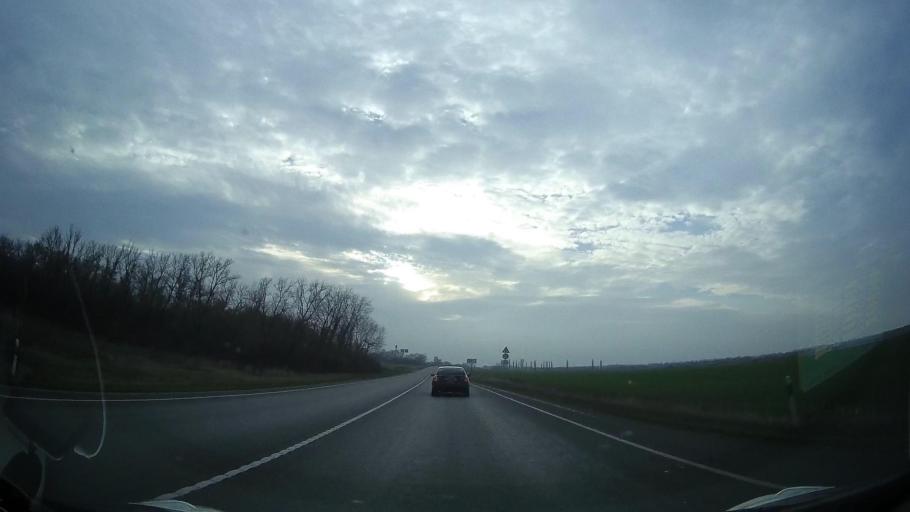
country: RU
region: Rostov
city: Ol'ginskaya
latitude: 47.1403
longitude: 39.9964
